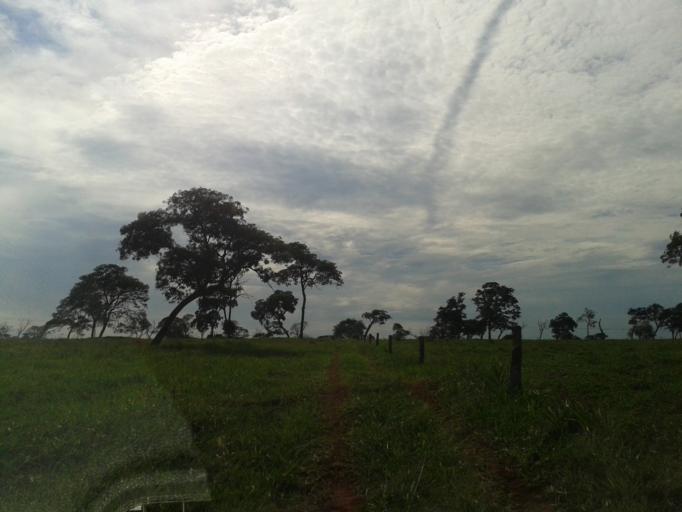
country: BR
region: Minas Gerais
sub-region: Santa Vitoria
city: Santa Vitoria
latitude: -19.2072
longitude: -50.6586
